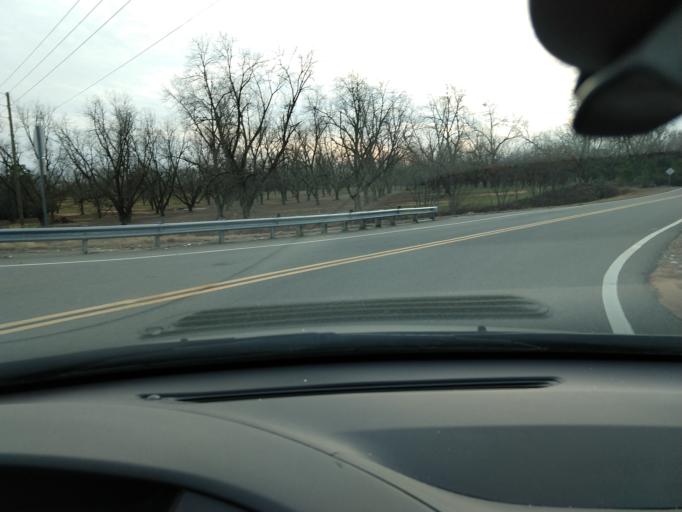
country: US
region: Georgia
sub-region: Sumter County
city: Americus
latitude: 32.0468
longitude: -84.2545
